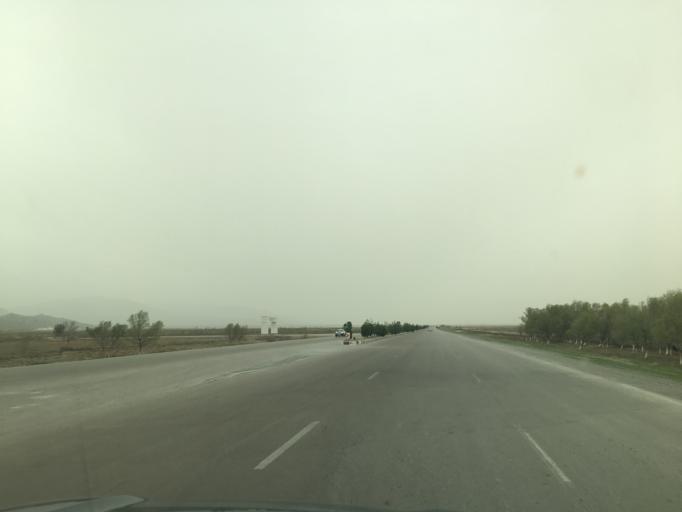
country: TM
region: Ahal
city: Baharly
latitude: 38.3479
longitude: 57.5530
